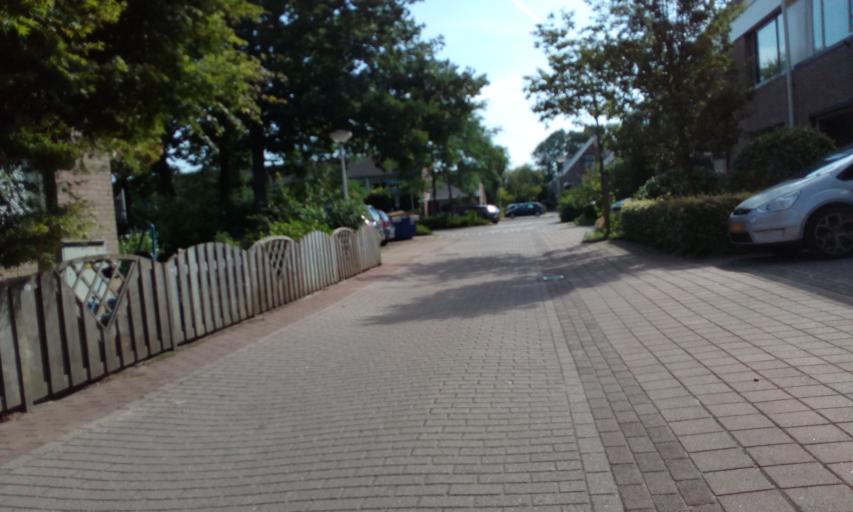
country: NL
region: South Holland
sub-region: Gemeente Pijnacker-Nootdorp
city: Pijnacker
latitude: 52.0087
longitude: 4.4413
